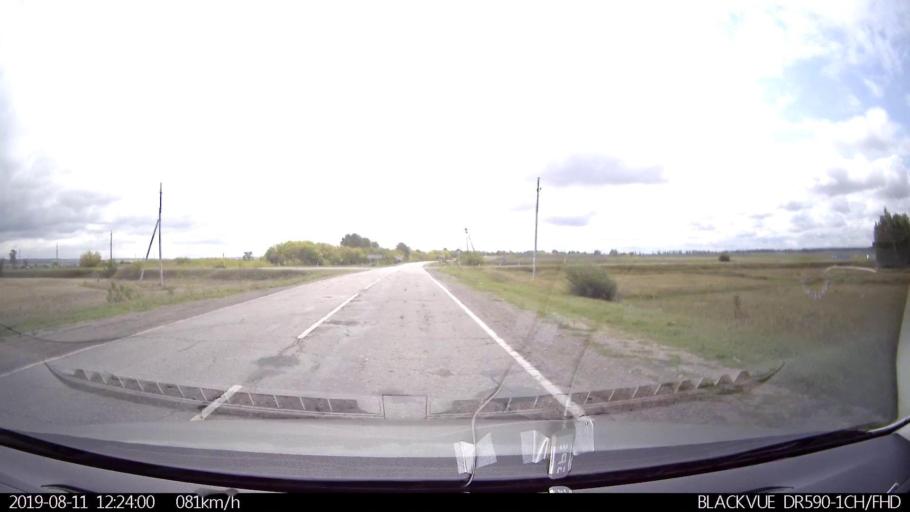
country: RU
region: Ulyanovsk
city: Ignatovka
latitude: 53.8884
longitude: 47.9502
